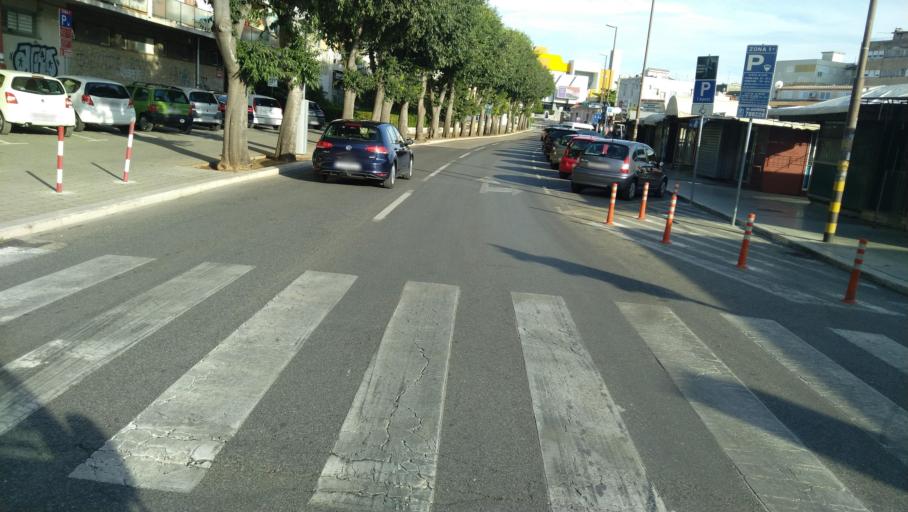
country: HR
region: Sibensko-Kniniska
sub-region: Grad Sibenik
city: Sibenik
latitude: 43.7330
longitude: 15.8958
